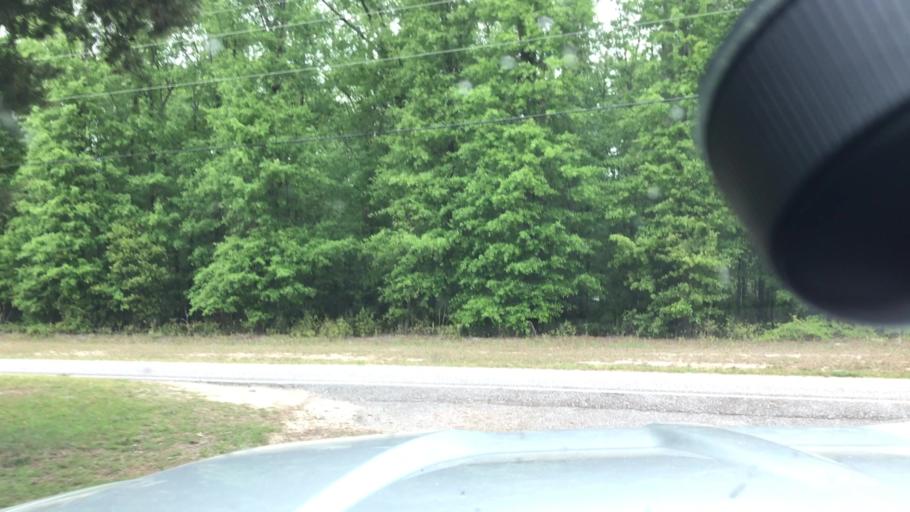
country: US
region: South Carolina
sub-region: Aiken County
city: Jackson
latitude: 33.3728
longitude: -81.8626
